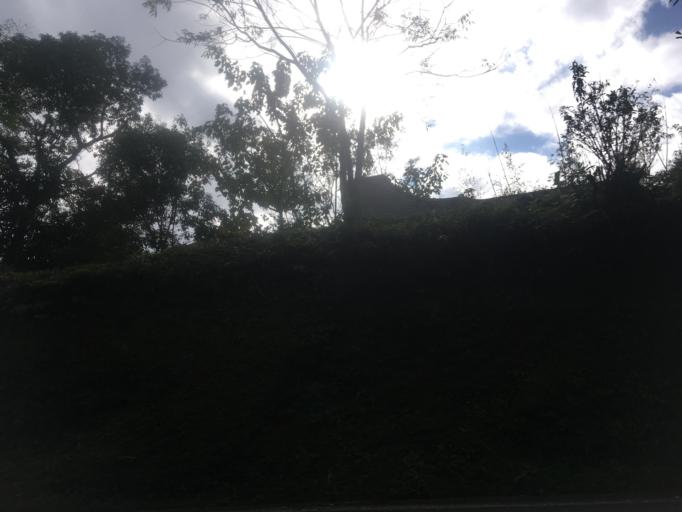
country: TW
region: Taiwan
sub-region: Yilan
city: Yilan
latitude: 24.6501
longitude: 121.5766
